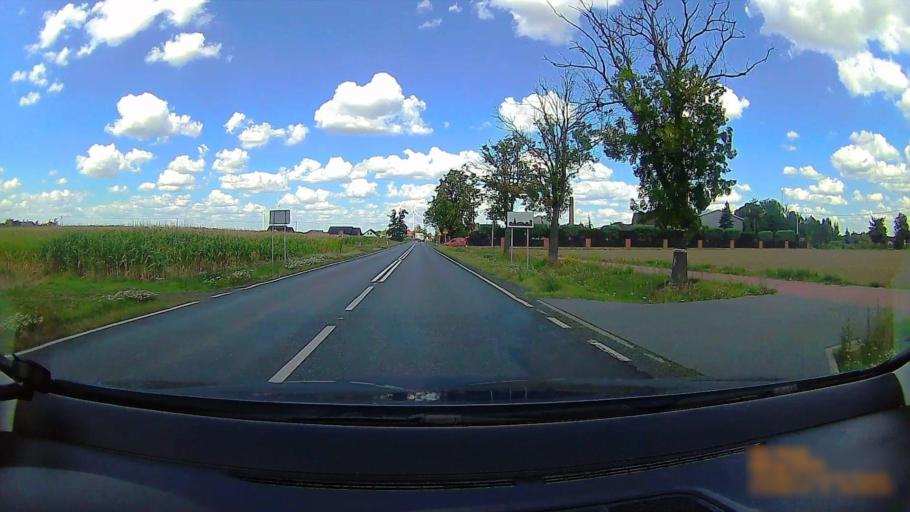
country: PL
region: Greater Poland Voivodeship
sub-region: Powiat koninski
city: Rychwal
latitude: 52.1136
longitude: 18.1676
